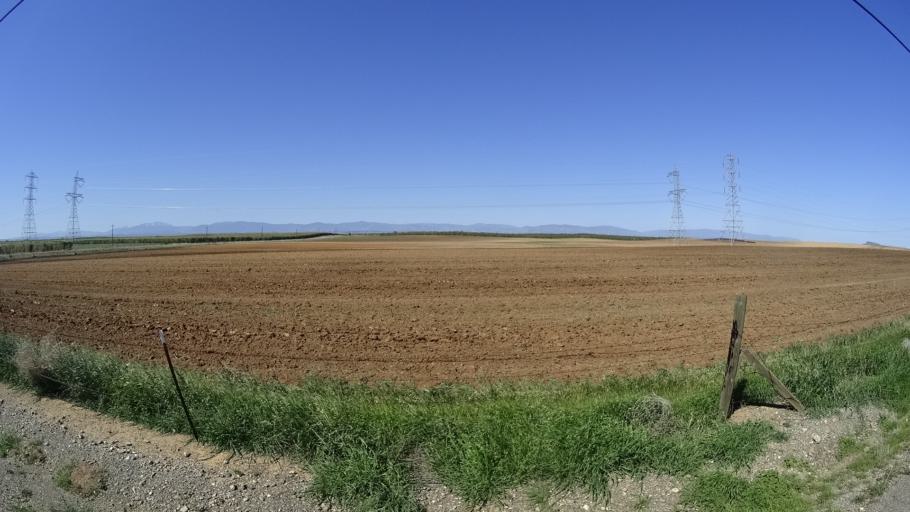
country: US
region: California
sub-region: Glenn County
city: Orland
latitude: 39.6696
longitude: -122.2718
